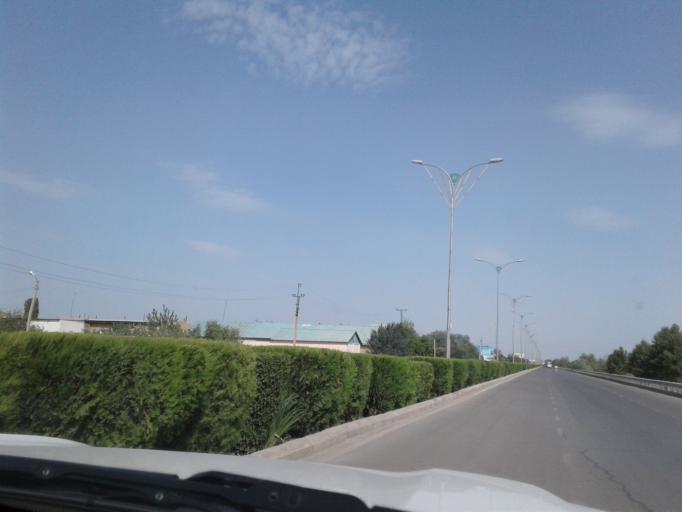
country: TM
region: Dasoguz
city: Dasoguz
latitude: 41.8334
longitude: 59.9351
